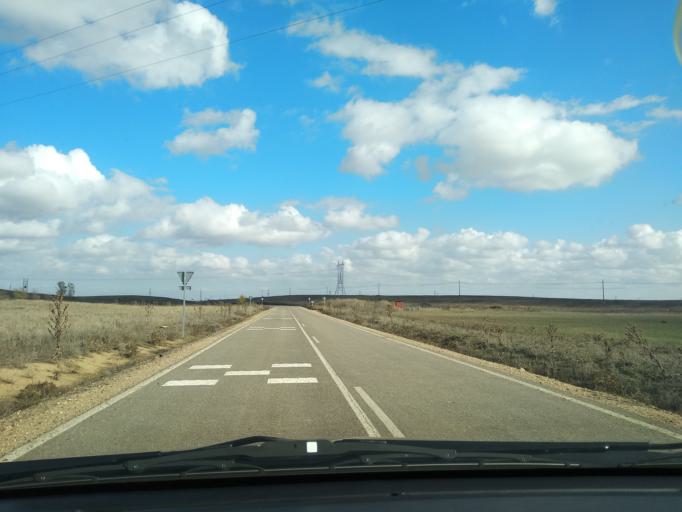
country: ES
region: Castille and Leon
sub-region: Provincia de Valladolid
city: Berrueces
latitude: 41.9467
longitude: -5.0929
